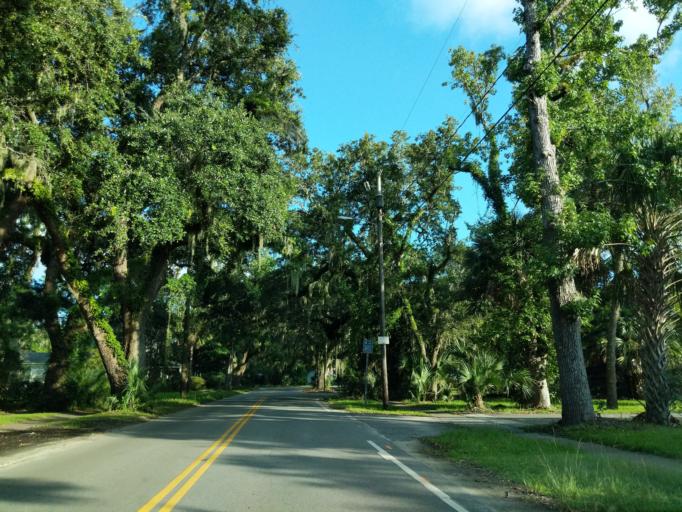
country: US
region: South Carolina
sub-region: Charleston County
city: Awendaw
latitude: 33.0886
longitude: -79.4616
